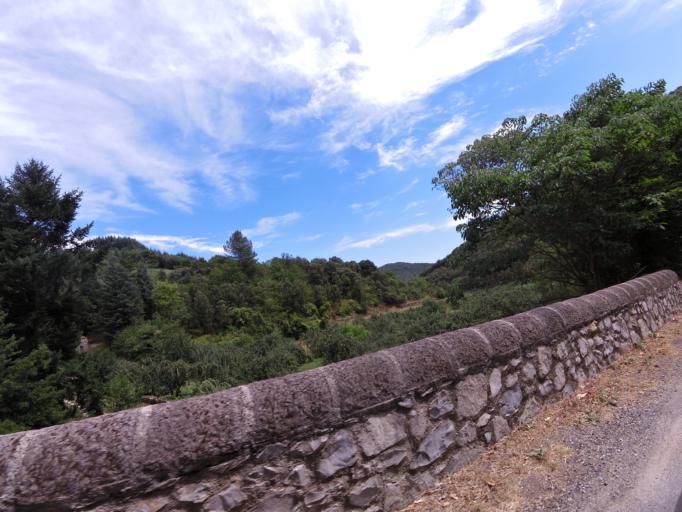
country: FR
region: Languedoc-Roussillon
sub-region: Departement du Gard
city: Le Vigan
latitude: 44.0099
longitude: 3.6476
